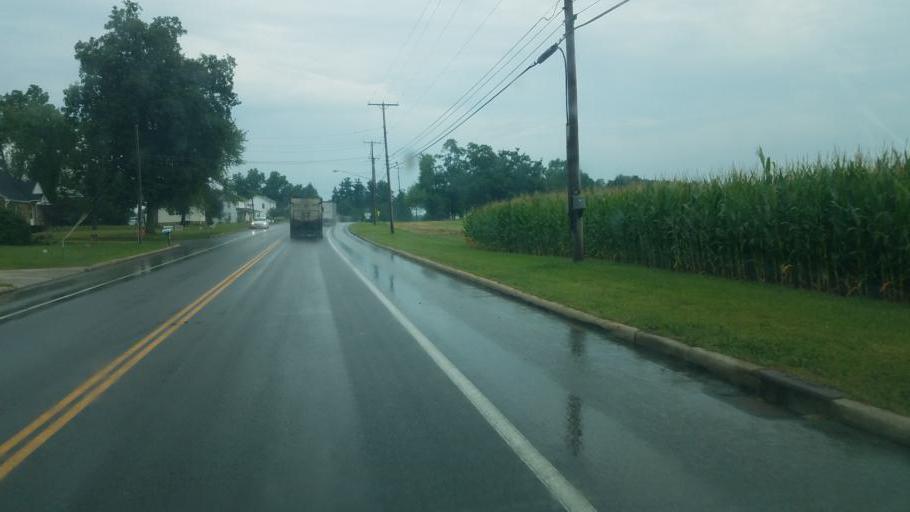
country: US
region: Ohio
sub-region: Geauga County
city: Middlefield
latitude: 41.3776
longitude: -81.0641
